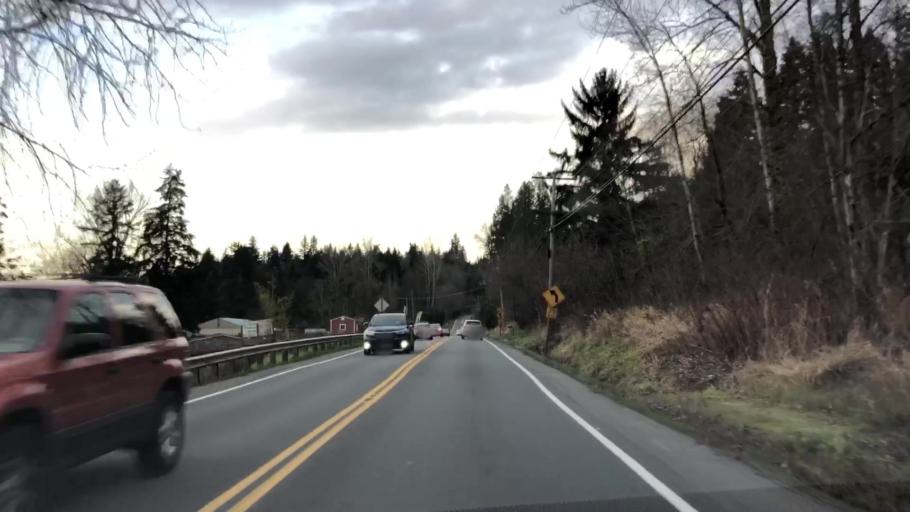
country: US
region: Washington
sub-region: King County
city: Woodinville
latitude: 47.7369
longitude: -122.1421
